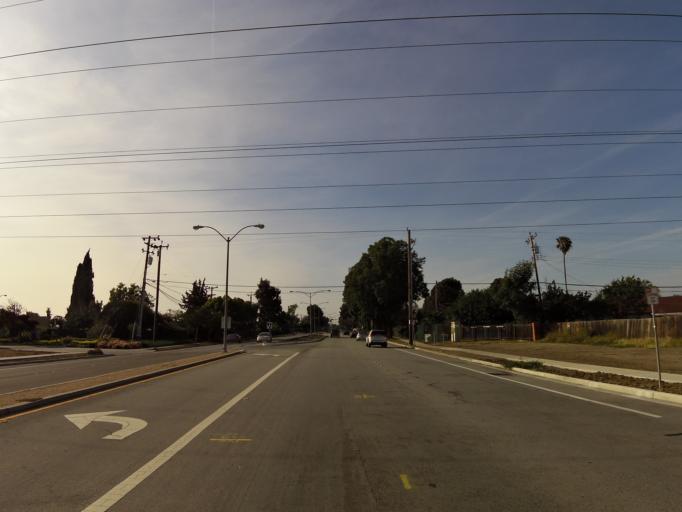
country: US
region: California
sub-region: Alameda County
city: Fremont
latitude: 37.5110
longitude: -121.9640
